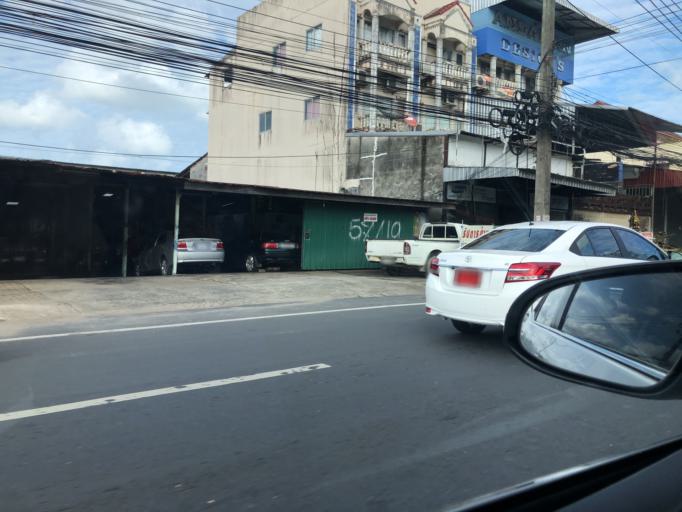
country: TH
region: Phuket
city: Ban Ko Kaeo
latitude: 7.9486
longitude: 98.3915
